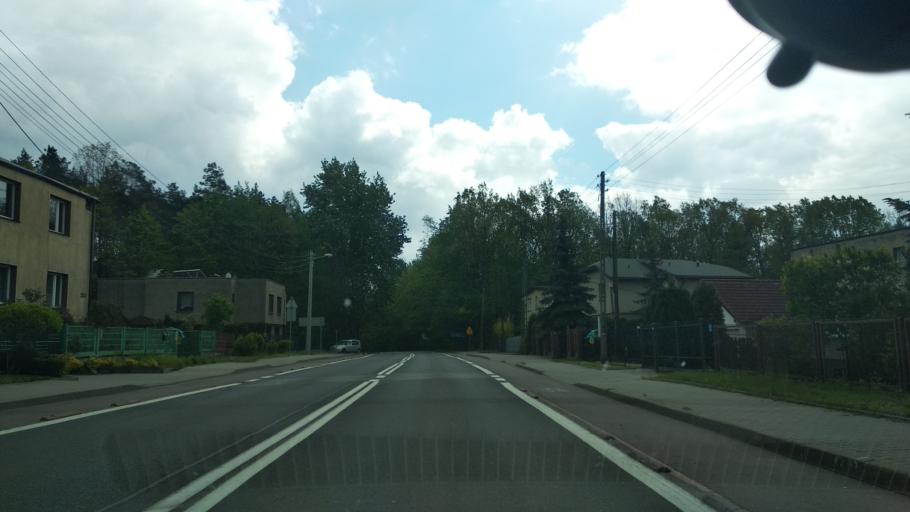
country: PL
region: Silesian Voivodeship
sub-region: Ruda Slaska
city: Ruda Slaska
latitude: 50.2374
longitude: 18.9094
